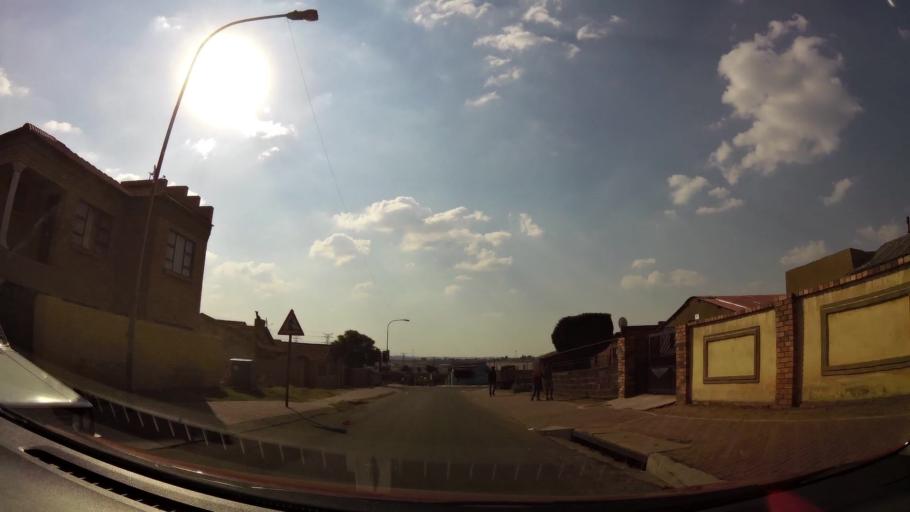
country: ZA
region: Gauteng
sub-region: City of Johannesburg Metropolitan Municipality
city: Soweto
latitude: -26.2359
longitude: 27.9432
